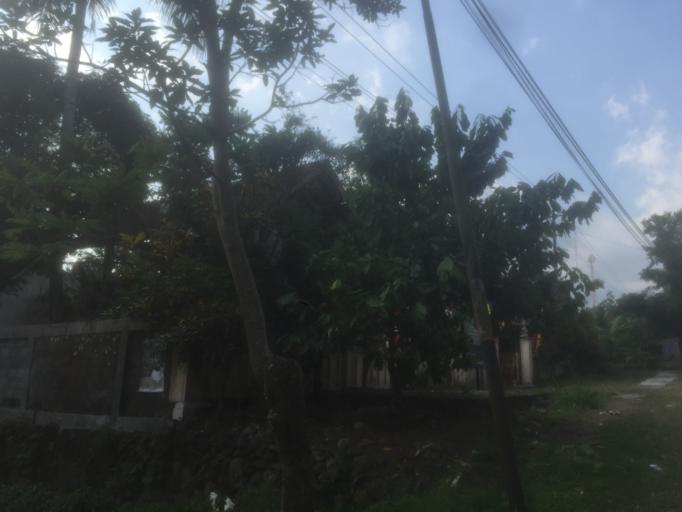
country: ID
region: Daerah Istimewa Yogyakarta
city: Sleman
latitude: -7.6417
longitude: 110.4251
